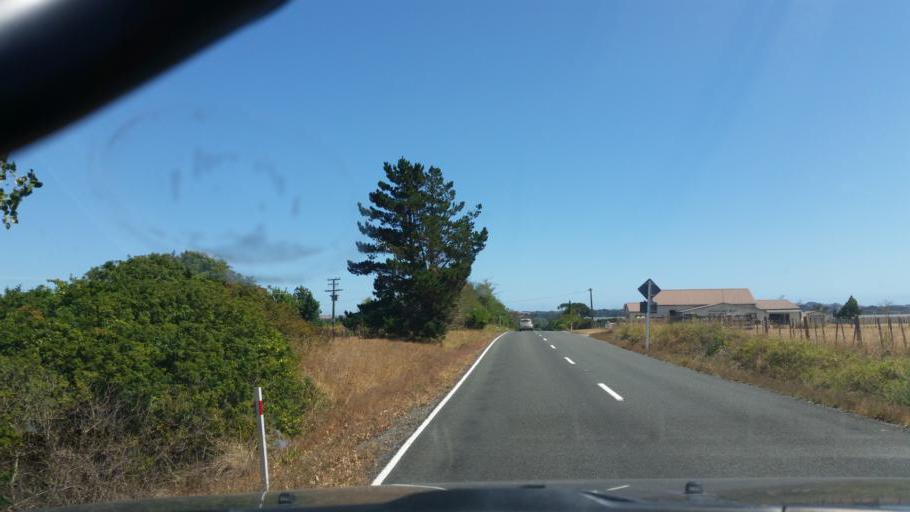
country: NZ
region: Northland
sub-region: Kaipara District
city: Dargaville
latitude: -36.0110
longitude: 173.9392
